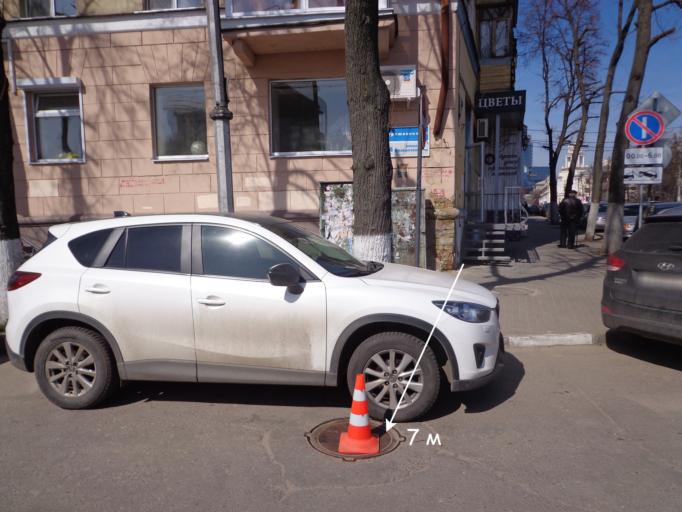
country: RU
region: Voronezj
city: Voronezh
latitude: 51.6643
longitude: 39.2114
